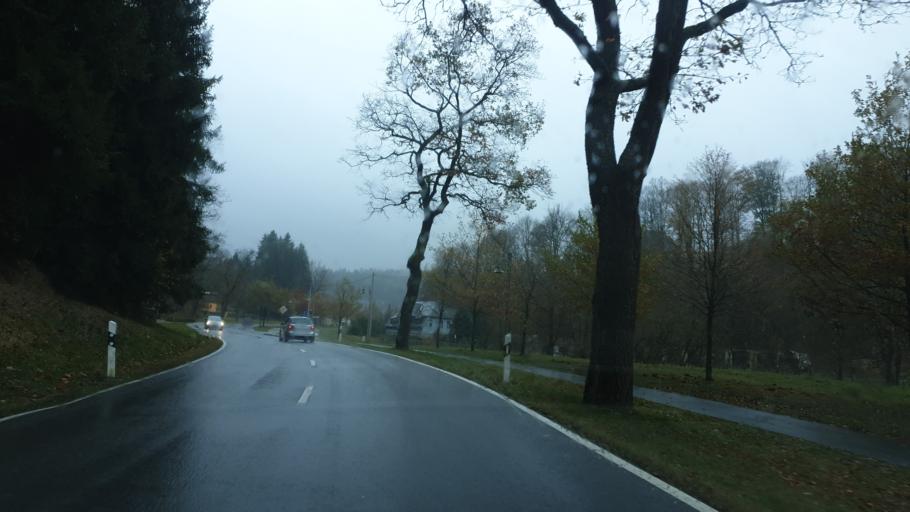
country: DE
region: Saxony
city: Tannenbergsthal
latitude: 50.4409
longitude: 12.4633
